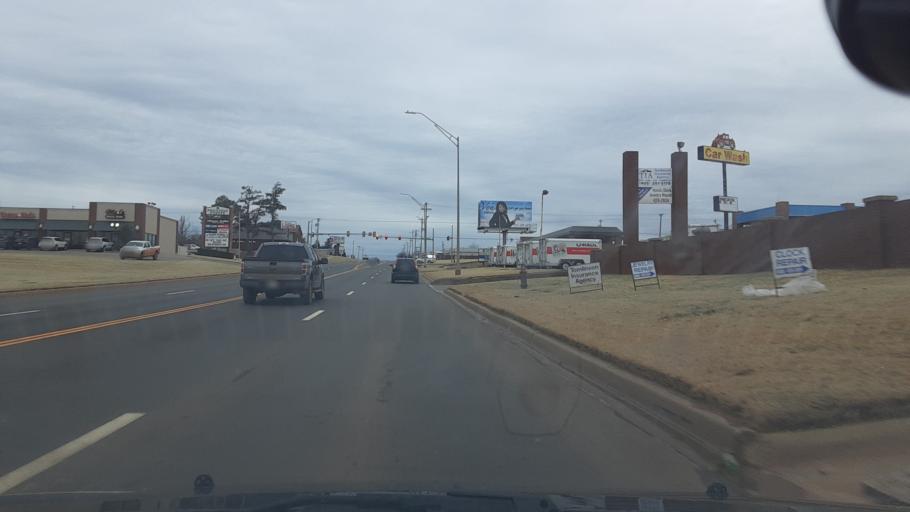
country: US
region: Oklahoma
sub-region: Logan County
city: Guthrie
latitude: 35.8579
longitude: -97.4255
